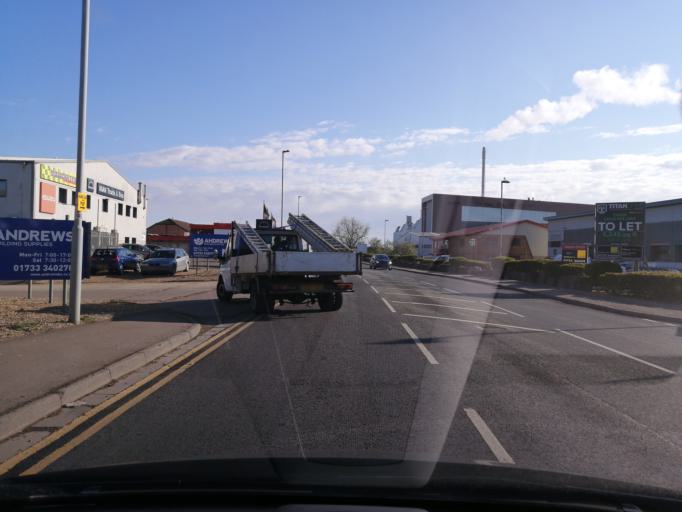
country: GB
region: England
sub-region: Peterborough
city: Peterborough
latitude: 52.5739
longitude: -0.2100
